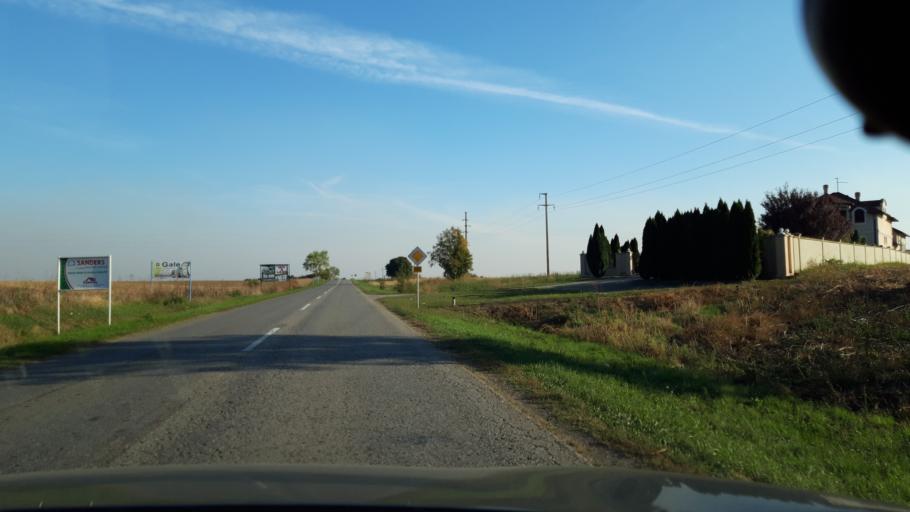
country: RS
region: Autonomna Pokrajina Vojvodina
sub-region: Sremski Okrug
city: Ruma
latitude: 45.0000
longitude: 19.8464
